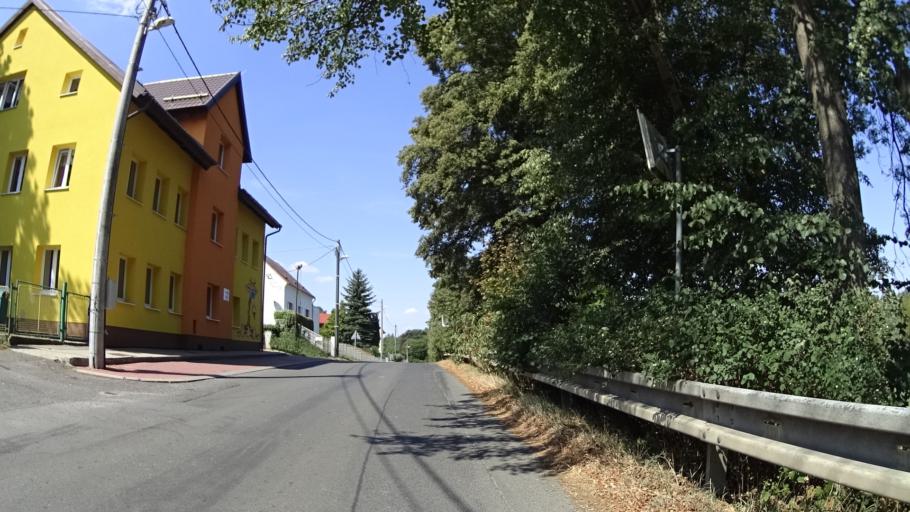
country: CZ
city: Hradek nad Nisou
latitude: 50.8350
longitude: 14.8661
